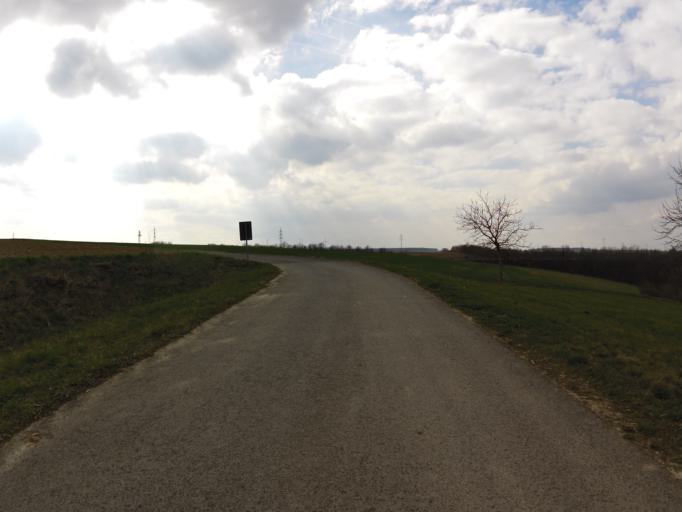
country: DE
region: Bavaria
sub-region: Regierungsbezirk Unterfranken
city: Buchbrunn
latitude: 49.7446
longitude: 10.1122
